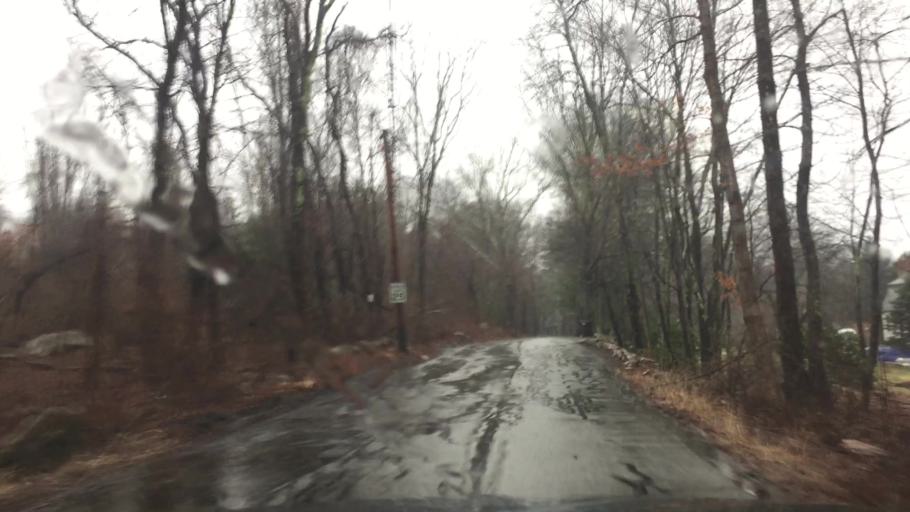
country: US
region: Massachusetts
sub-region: Middlesex County
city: Ashland
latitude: 42.2309
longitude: -71.4650
